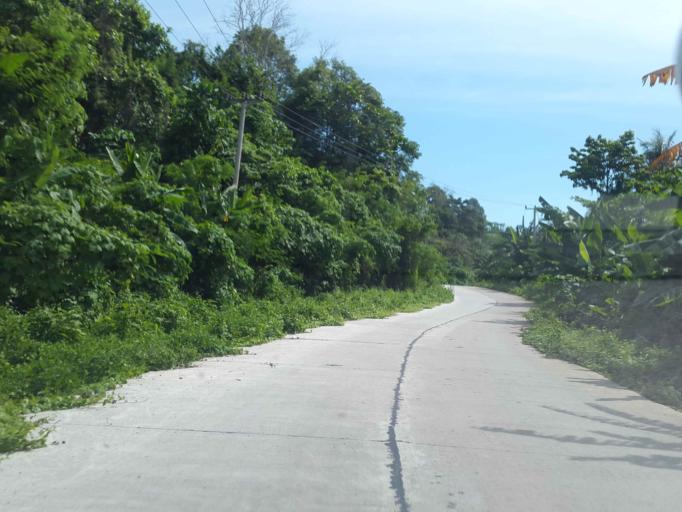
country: ID
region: Banten
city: Babakanbungur
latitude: -6.5134
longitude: 105.6352
